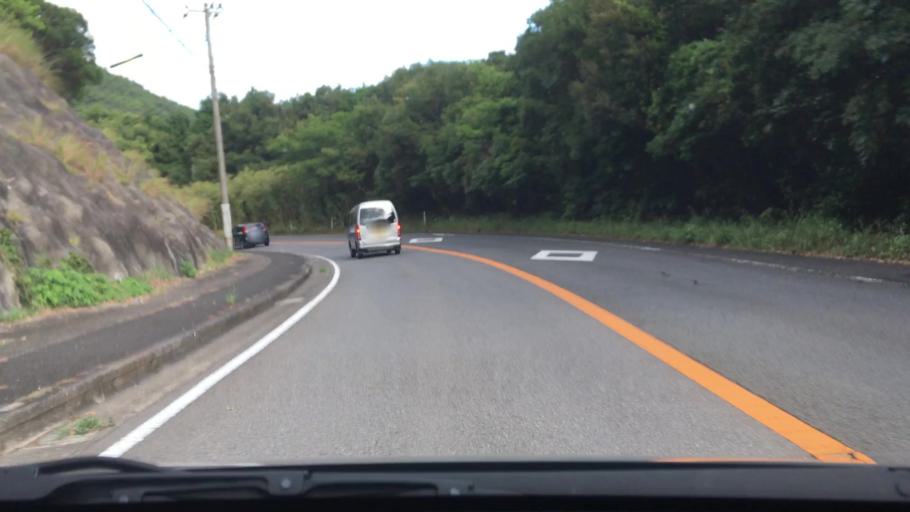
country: JP
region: Nagasaki
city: Togitsu
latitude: 32.8216
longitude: 129.7311
